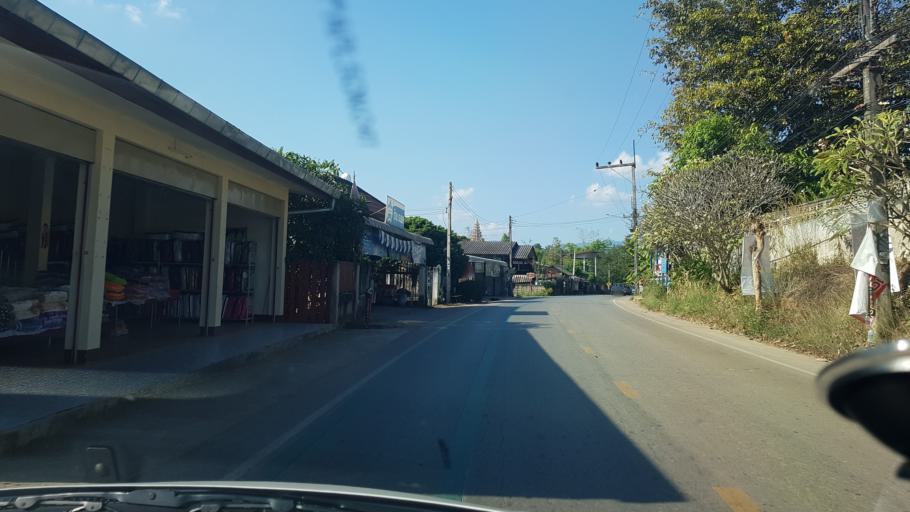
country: TH
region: Chiang Rai
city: Chiang Rai
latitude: 19.9436
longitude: 99.8112
